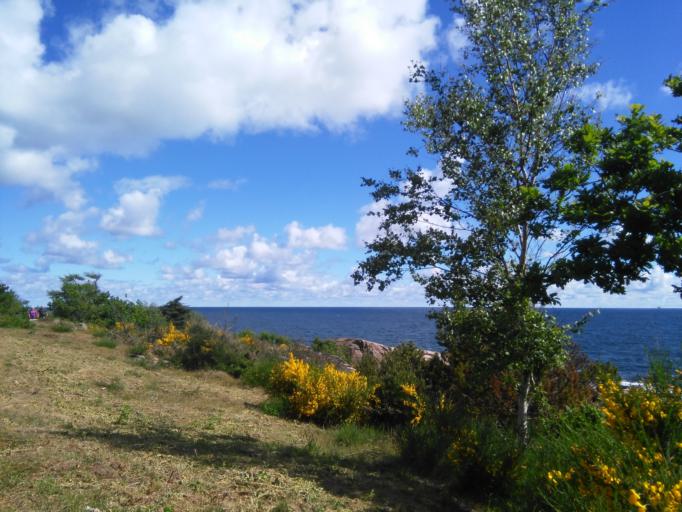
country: DK
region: Capital Region
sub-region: Bornholm Kommune
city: Ronne
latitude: 55.2942
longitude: 14.7776
